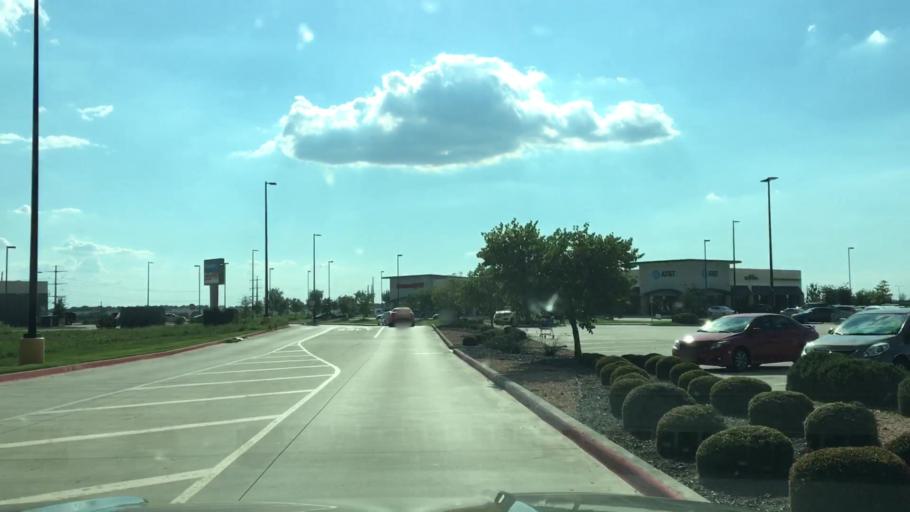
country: US
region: Texas
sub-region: Tarrant County
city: Pecan Acres
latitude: 32.9663
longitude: -97.4125
